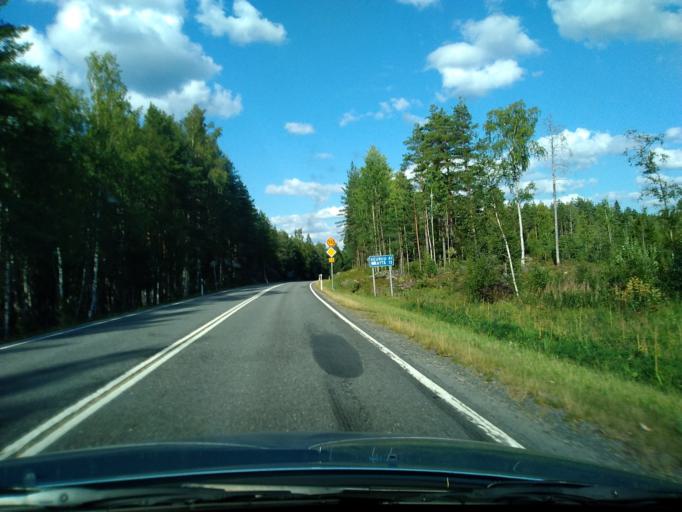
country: FI
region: Pirkanmaa
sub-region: Ylae-Pirkanmaa
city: Vilppula
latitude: 61.9505
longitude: 24.5460
